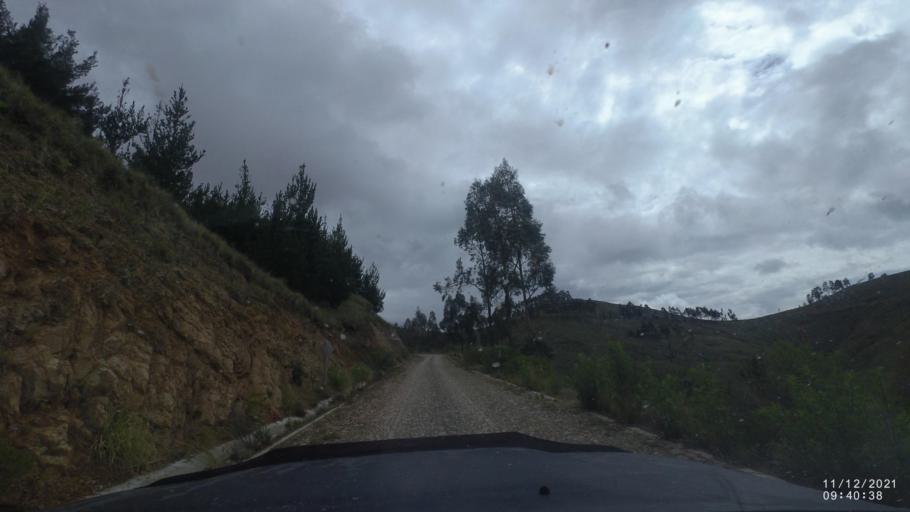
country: BO
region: Cochabamba
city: Tarata
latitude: -17.8152
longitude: -65.9817
